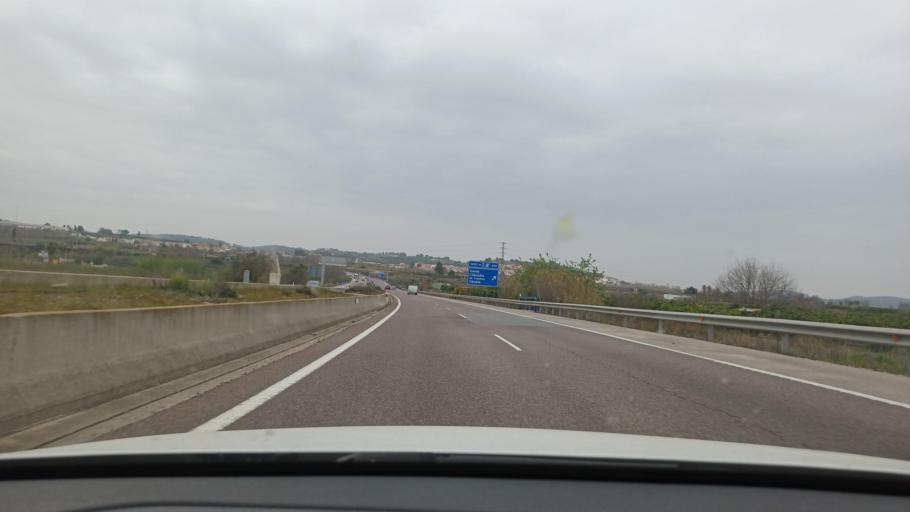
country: ES
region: Valencia
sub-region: Provincia de Valencia
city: Cerda
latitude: 38.9745
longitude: -0.5659
